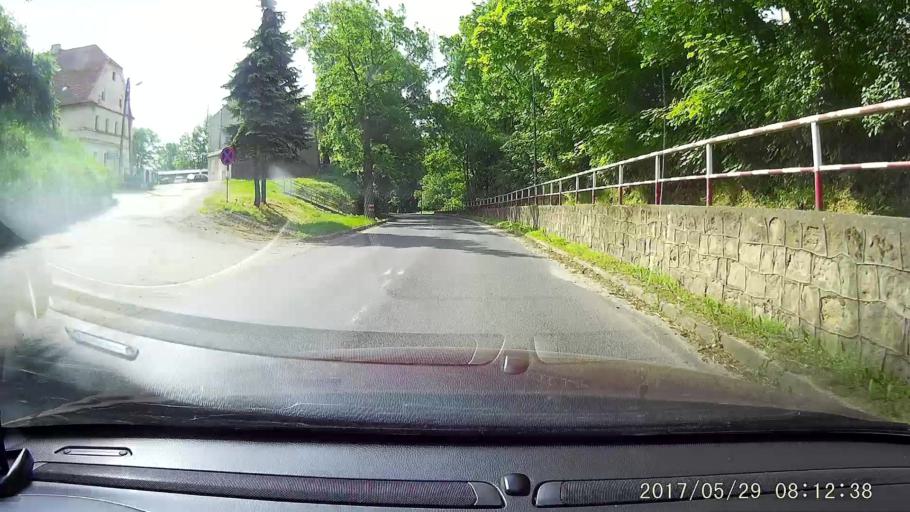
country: PL
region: Lower Silesian Voivodeship
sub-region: Powiat zlotoryjski
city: Zlotoryja
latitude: 51.1313
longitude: 15.9108
